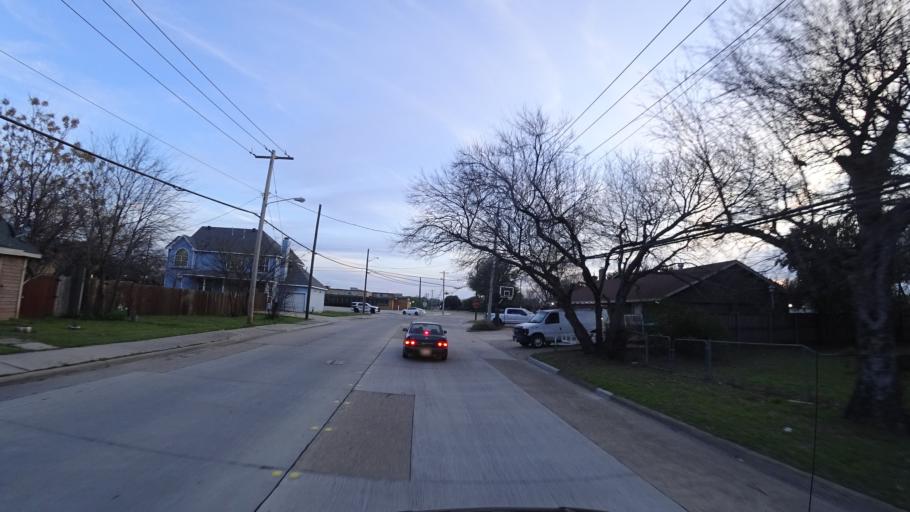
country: US
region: Texas
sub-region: Denton County
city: Lewisville
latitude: 33.0426
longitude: -96.9966
